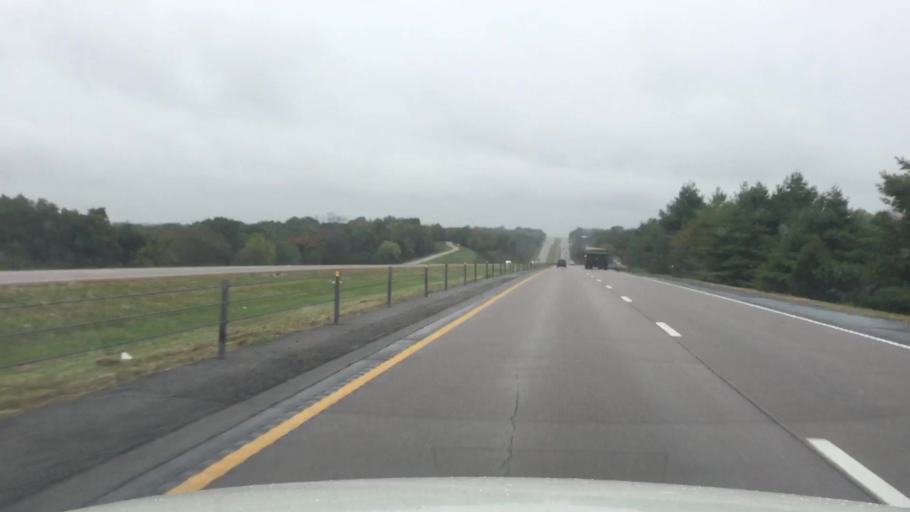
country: US
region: Missouri
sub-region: Boone County
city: Ashland
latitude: 38.7114
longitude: -92.2546
